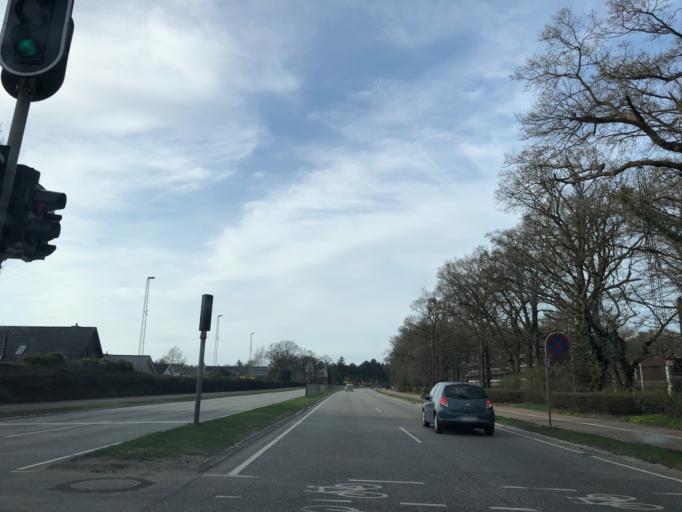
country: DK
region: Zealand
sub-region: Koge Kommune
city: Koge
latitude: 55.4516
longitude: 12.1741
